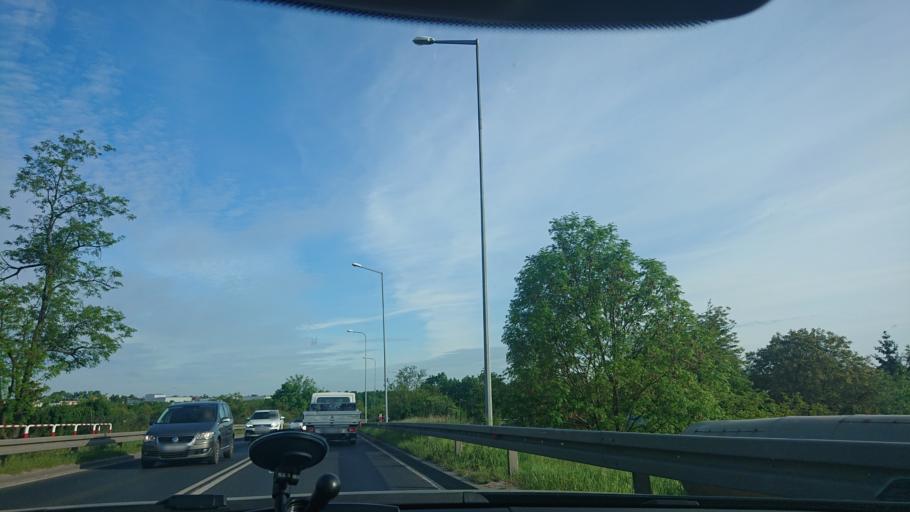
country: PL
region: Greater Poland Voivodeship
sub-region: Powiat gnieznienski
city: Gniezno
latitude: 52.5267
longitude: 17.5851
